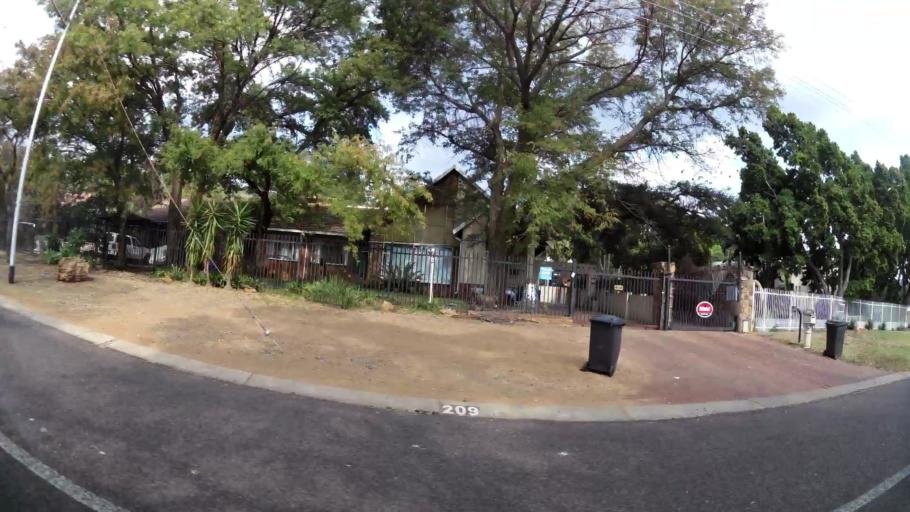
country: ZA
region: Gauteng
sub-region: City of Tshwane Metropolitan Municipality
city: Pretoria
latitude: -25.7553
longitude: 28.3008
